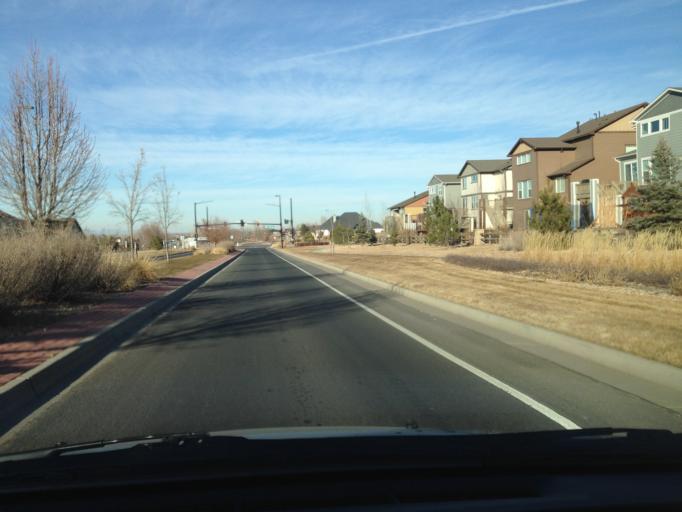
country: US
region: Colorado
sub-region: Boulder County
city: Erie
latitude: 40.0348
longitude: -105.0859
